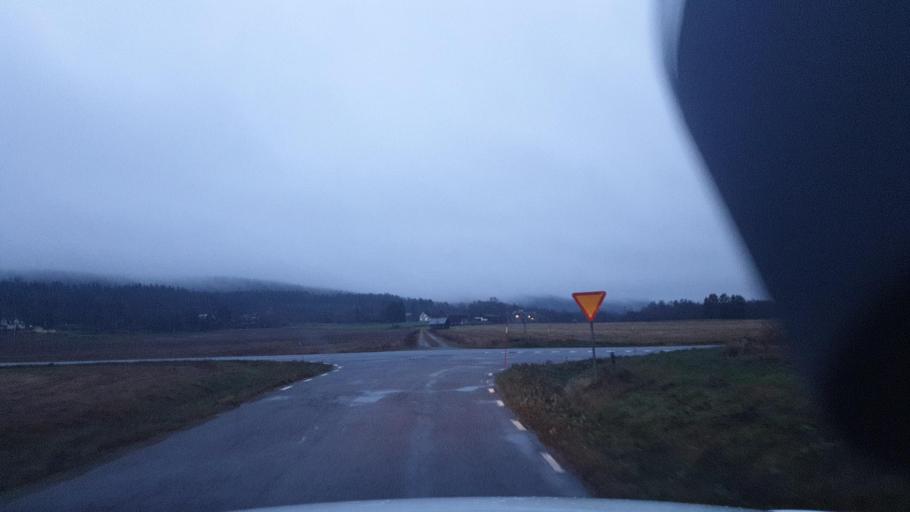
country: SE
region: Vaermland
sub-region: Eda Kommun
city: Amotfors
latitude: 59.6811
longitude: 12.1386
